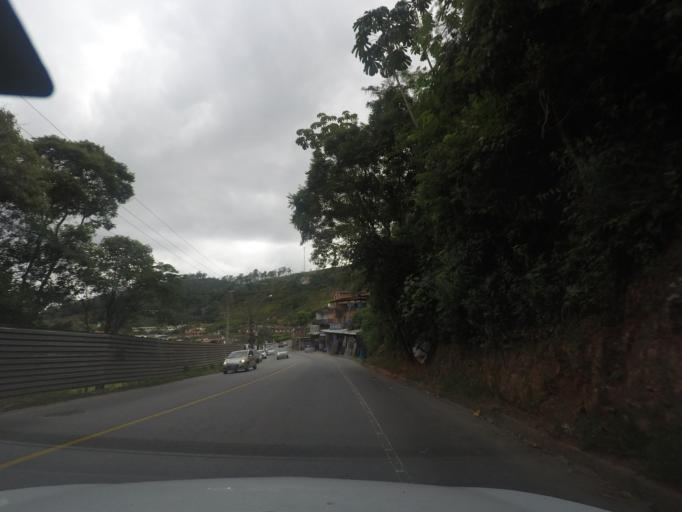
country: BR
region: Rio de Janeiro
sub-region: Teresopolis
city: Teresopolis
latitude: -22.3880
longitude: -42.9568
